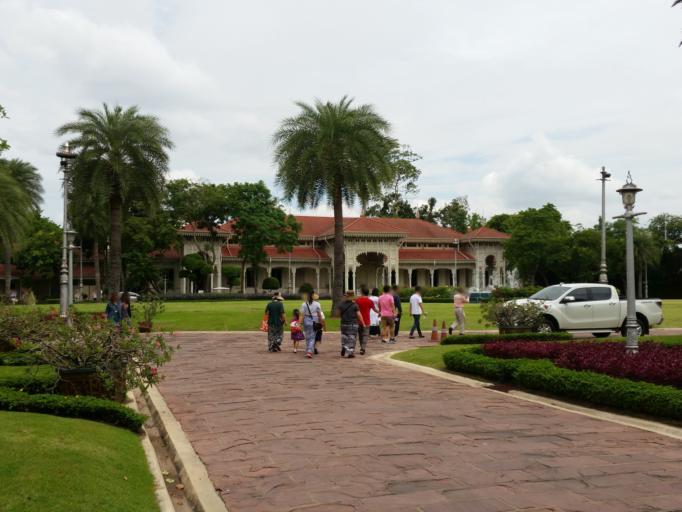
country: TH
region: Bangkok
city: Dusit
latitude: 13.7729
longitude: 100.5137
